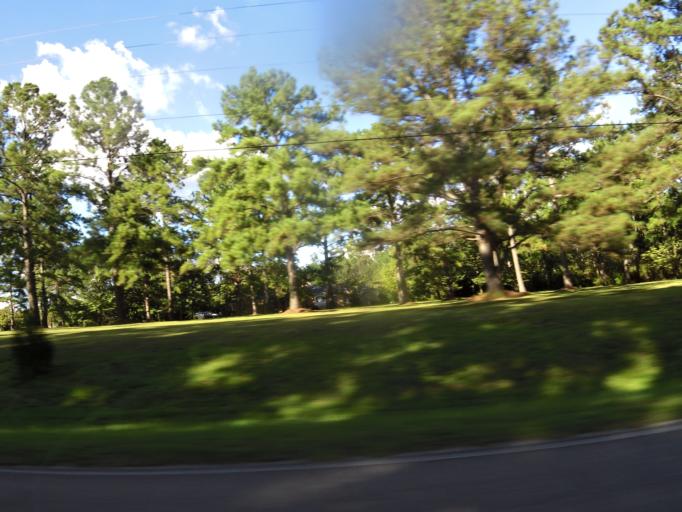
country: US
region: Florida
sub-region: Wakulla County
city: Crawfordville
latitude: 30.0680
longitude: -84.5051
